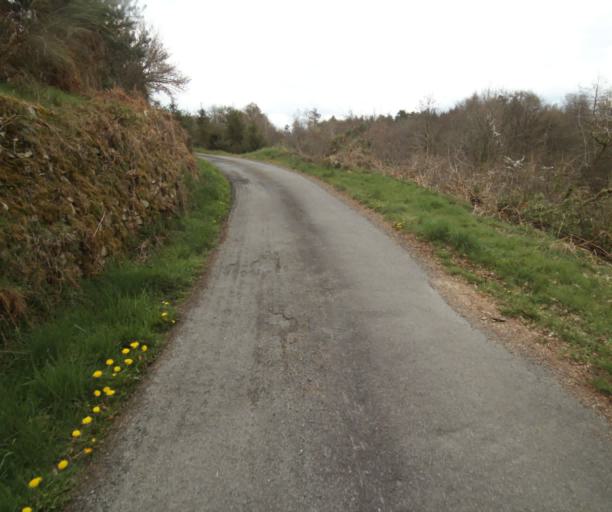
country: FR
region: Limousin
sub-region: Departement de la Correze
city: Correze
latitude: 45.3138
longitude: 1.8894
